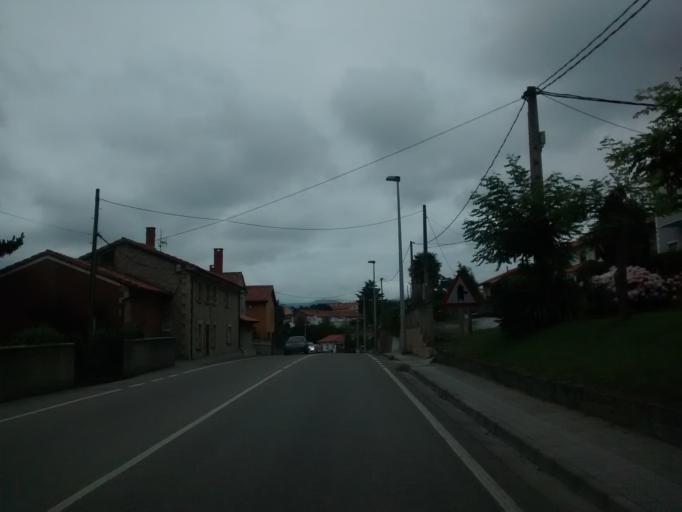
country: ES
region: Cantabria
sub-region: Provincia de Cantabria
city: Polanco
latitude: 43.3833
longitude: -4.0484
